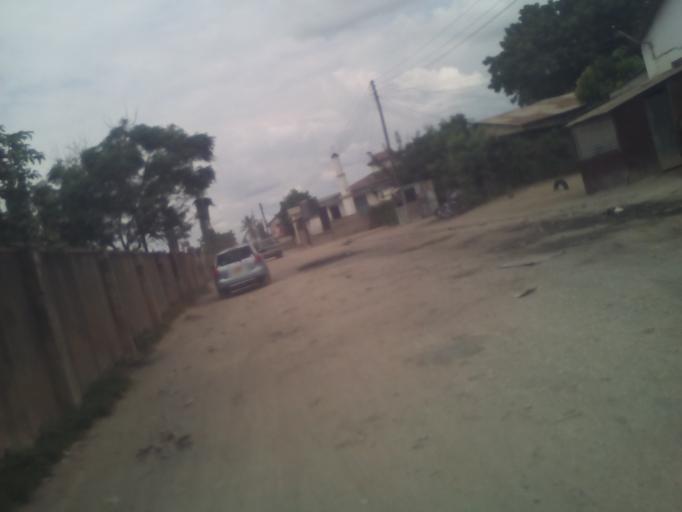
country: TZ
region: Dar es Salaam
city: Dar es Salaam
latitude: -6.8564
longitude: 39.2448
